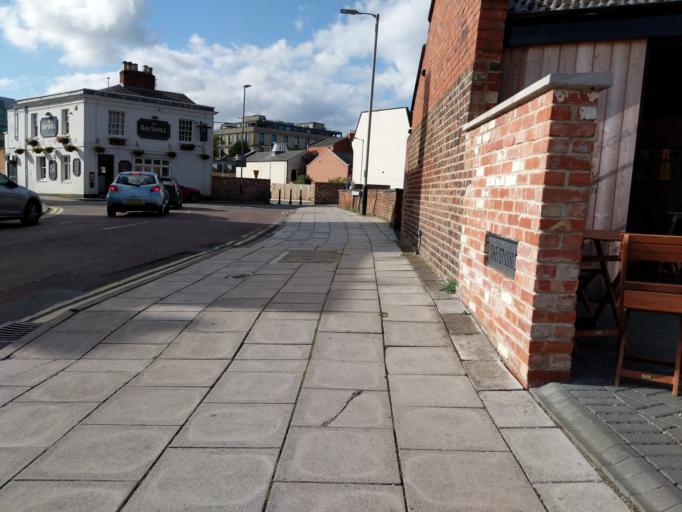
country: GB
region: England
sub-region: Gloucestershire
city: Cheltenham
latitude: 51.8995
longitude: -2.0798
